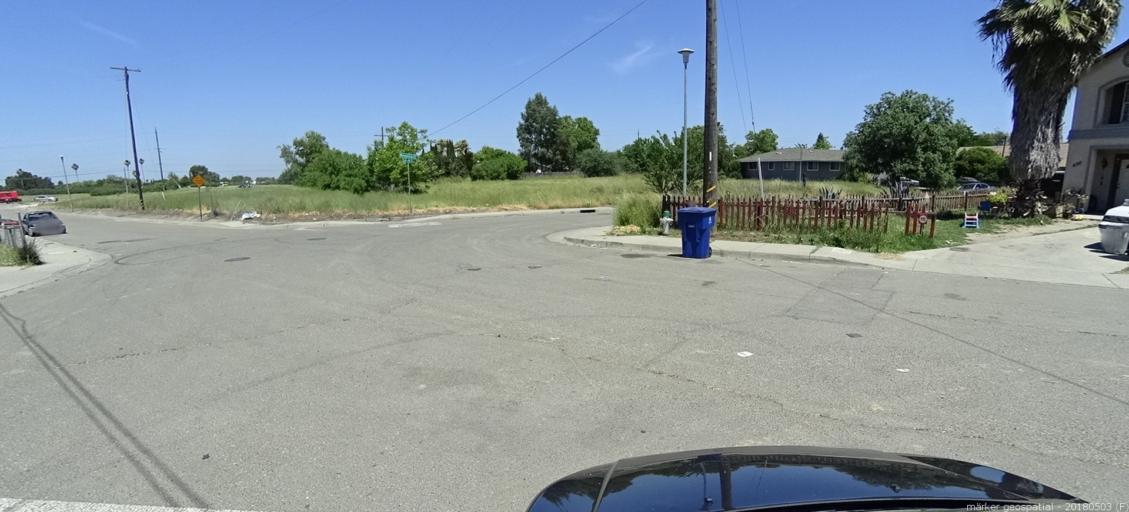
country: US
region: California
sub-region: Sacramento County
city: Rio Linda
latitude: 38.6458
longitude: -121.4337
